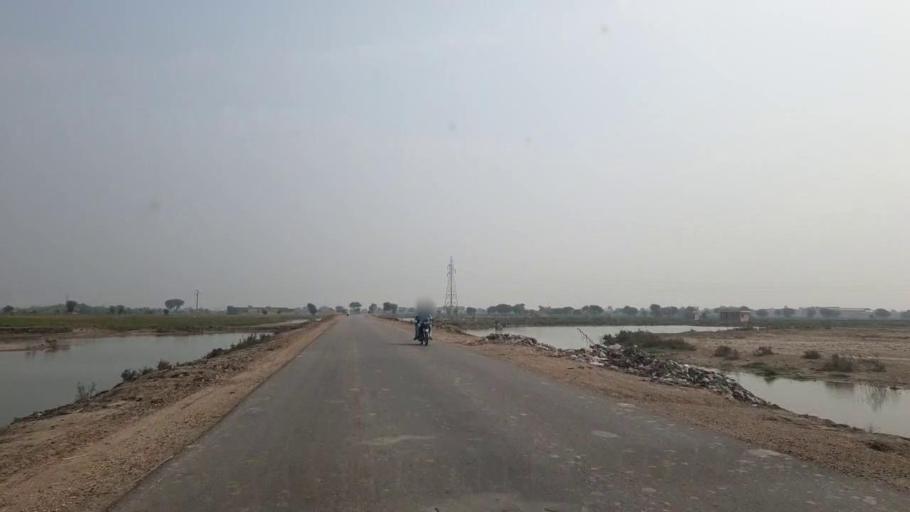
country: PK
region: Sindh
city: Matli
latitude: 25.0583
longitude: 68.6714
